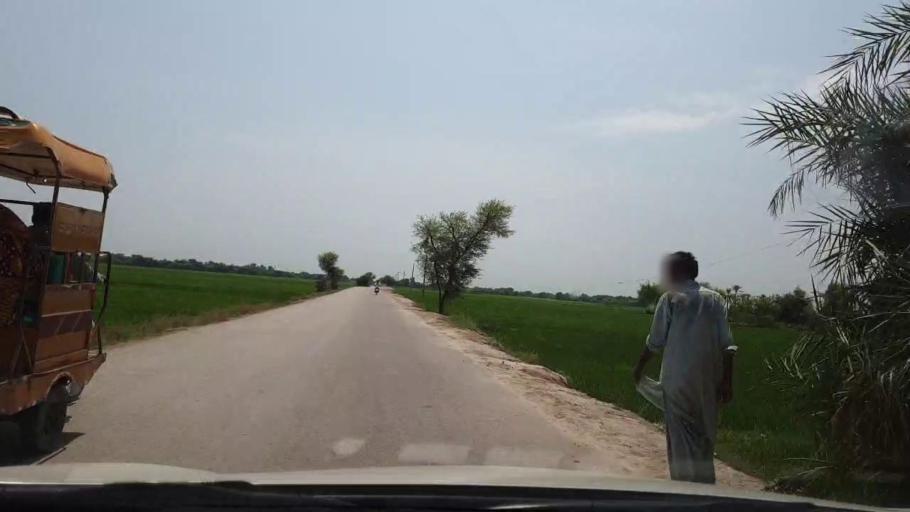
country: PK
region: Sindh
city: Ratodero
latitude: 27.8225
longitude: 68.2432
